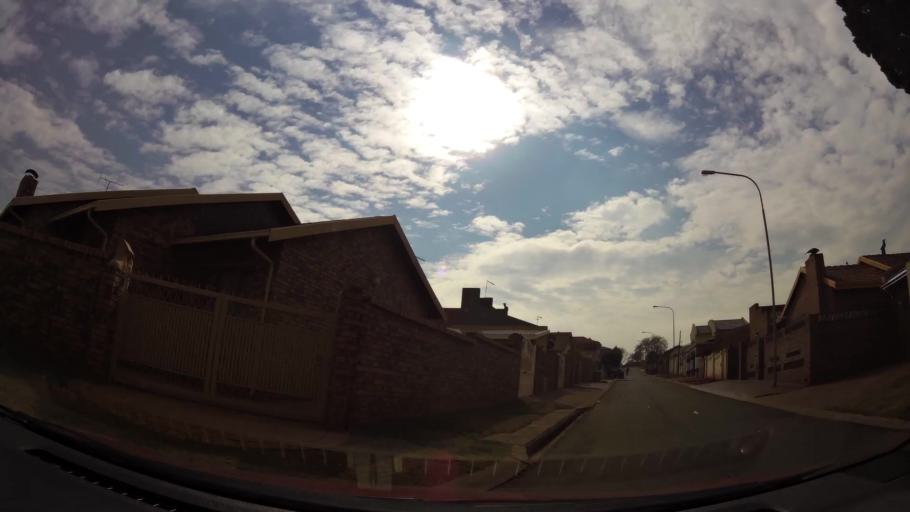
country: ZA
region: Gauteng
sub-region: City of Johannesburg Metropolitan Municipality
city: Soweto
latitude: -26.2680
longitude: 27.8256
